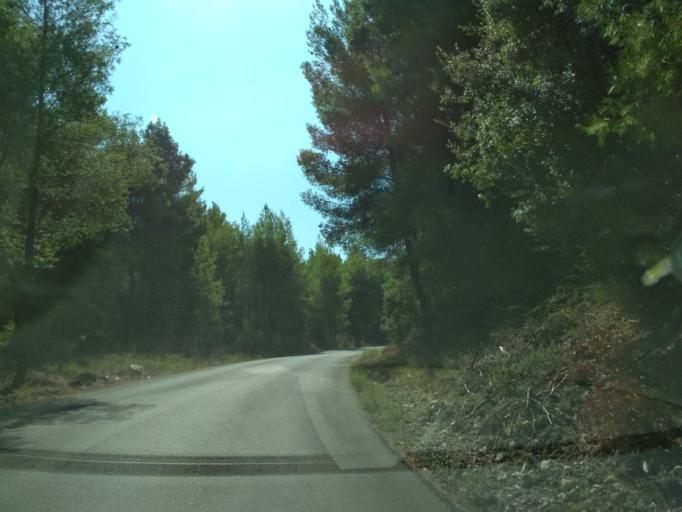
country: GR
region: Central Greece
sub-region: Nomos Evvoias
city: Roviai
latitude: 38.8173
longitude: 23.2733
